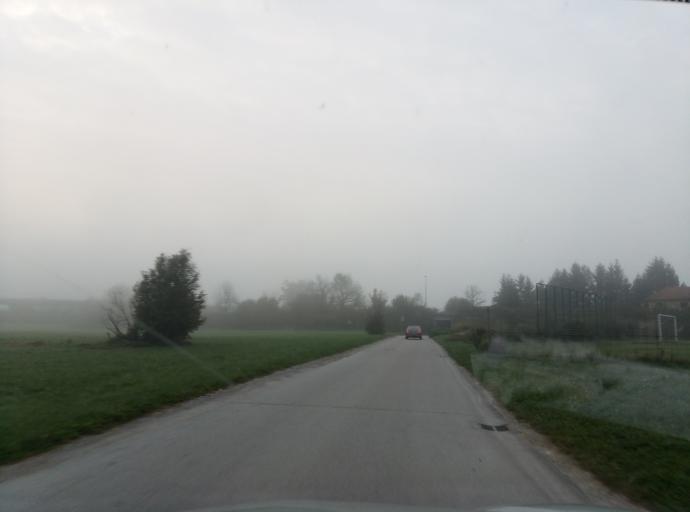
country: SI
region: Trzin
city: Trzin
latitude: 46.1028
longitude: 14.5359
